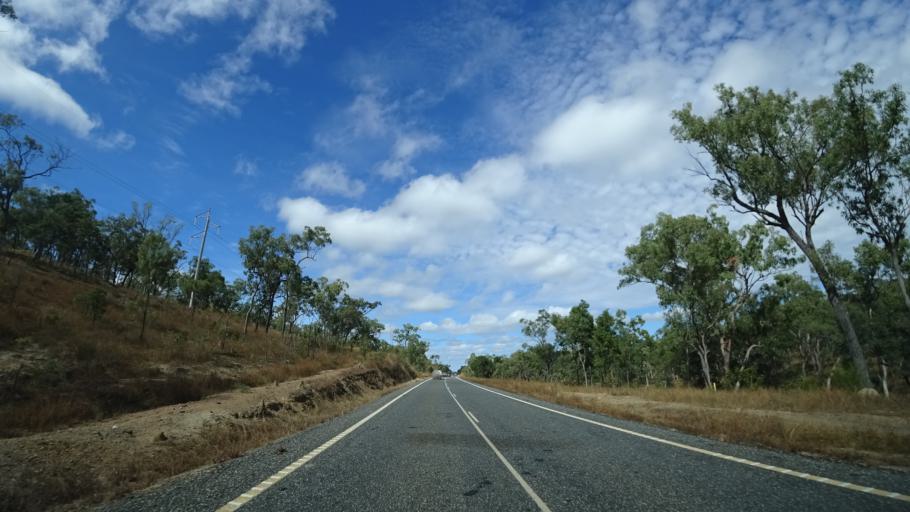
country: AU
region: Queensland
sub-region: Cairns
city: Port Douglas
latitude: -16.3079
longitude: 144.7172
